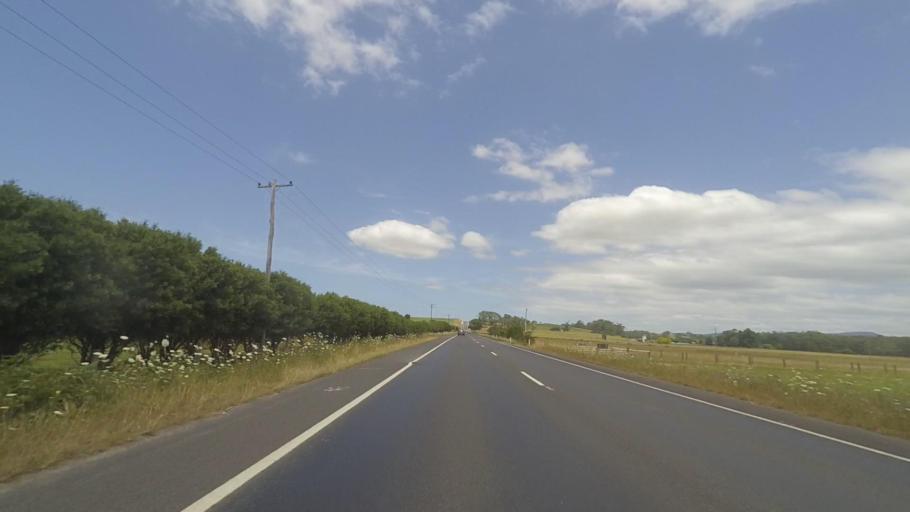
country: AU
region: New South Wales
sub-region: Shoalhaven Shire
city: Milton
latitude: -35.2772
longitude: 150.4233
